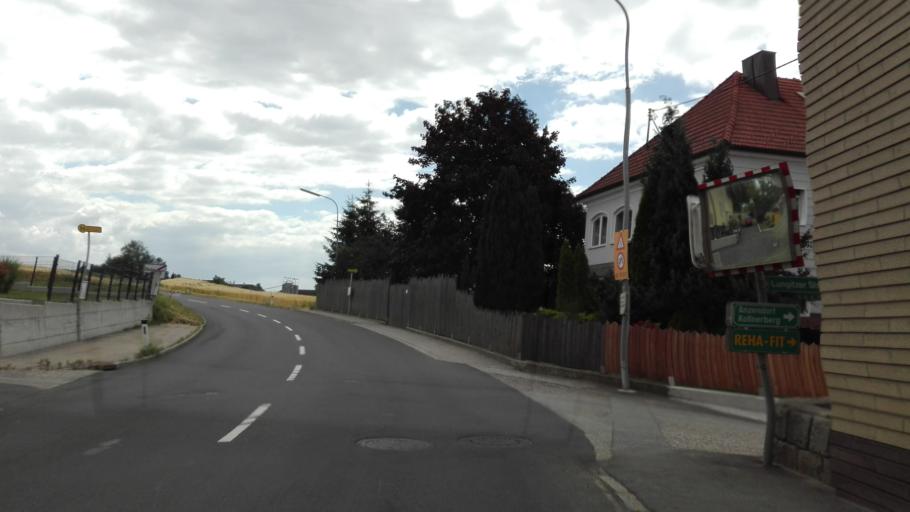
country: AT
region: Lower Austria
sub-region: Politischer Bezirk Amstetten
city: Ennsdorf
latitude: 48.2753
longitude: 14.5166
